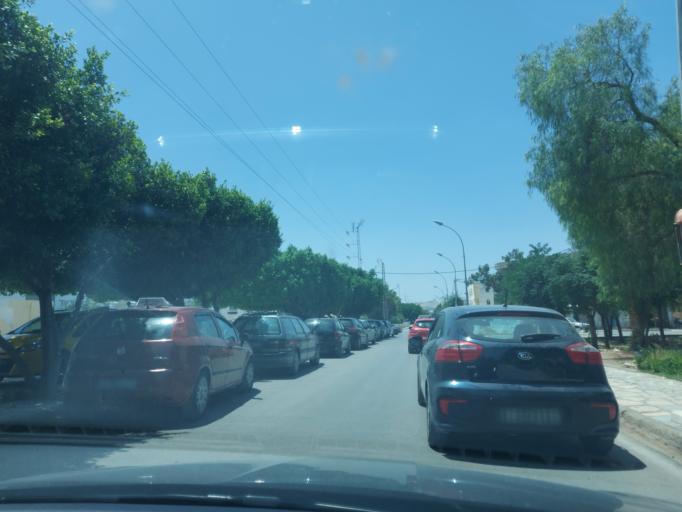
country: TN
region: Silyanah
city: Siliana
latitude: 36.0849
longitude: 9.3659
